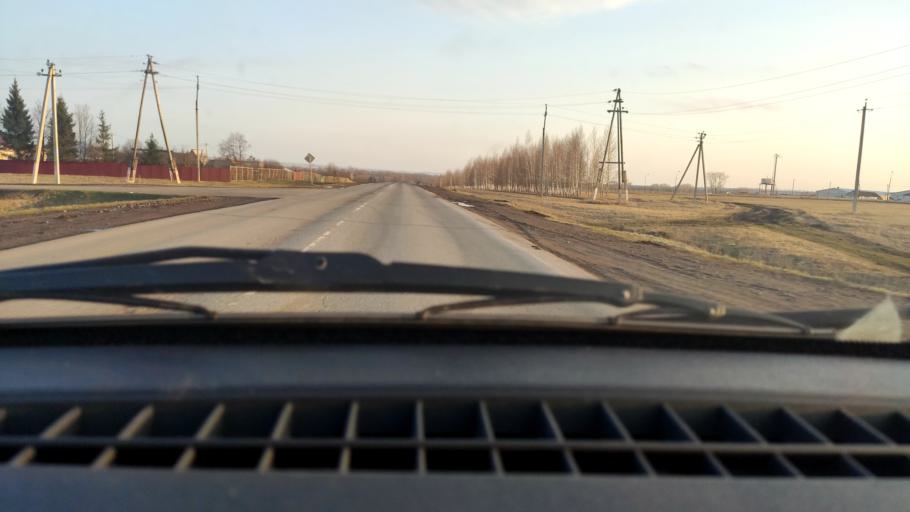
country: RU
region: Bashkortostan
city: Davlekanovo
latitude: 54.3778
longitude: 55.1956
